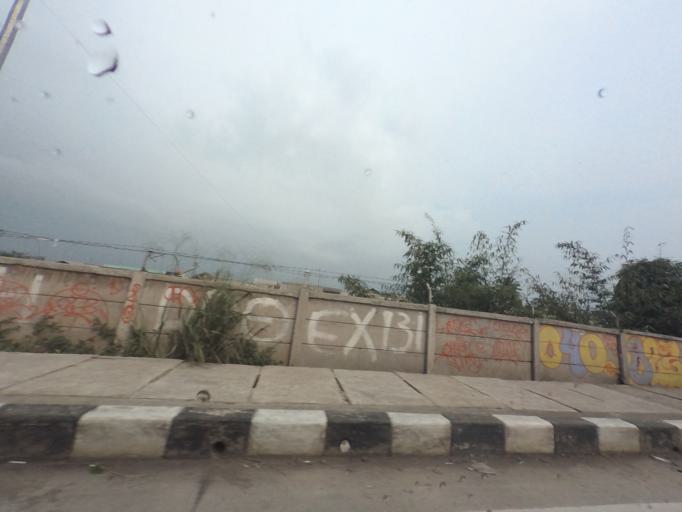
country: ID
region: West Java
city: Cicurug
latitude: -6.7525
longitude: 106.7996
